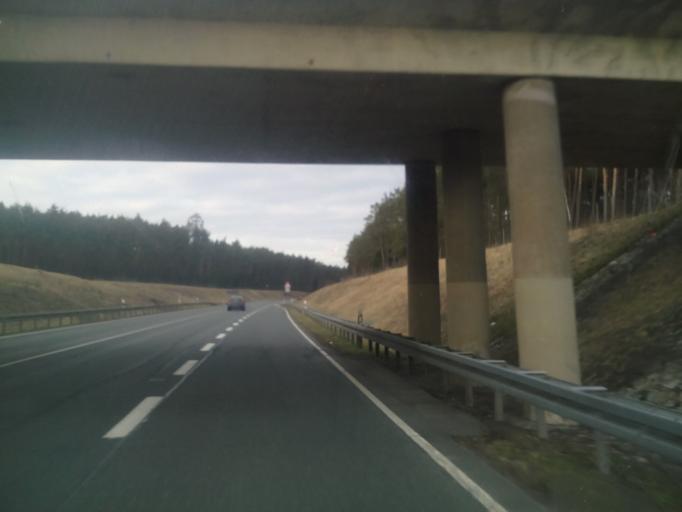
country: DE
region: Bavaria
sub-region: Upper Franconia
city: Pommersfelden
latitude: 49.7434
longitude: 10.8281
